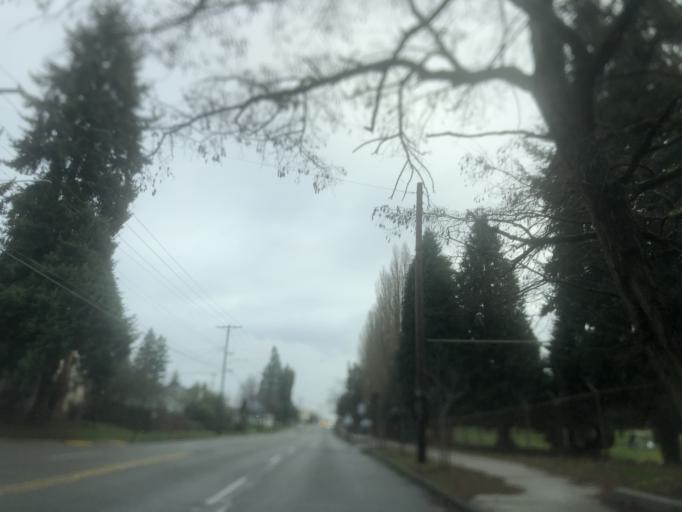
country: US
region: Washington
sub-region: Pierce County
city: Tacoma
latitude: 47.2430
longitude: -122.4735
